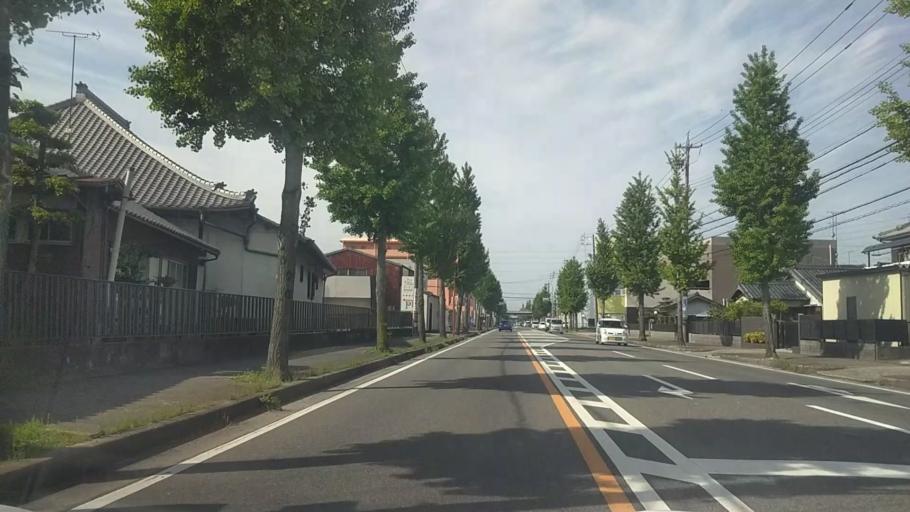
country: JP
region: Aichi
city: Okazaki
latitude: 34.9445
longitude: 137.1540
